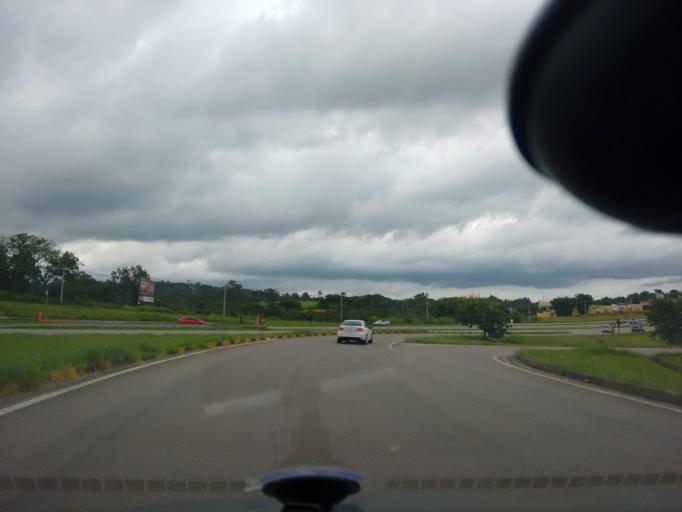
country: BR
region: Sao Paulo
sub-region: Indaiatuba
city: Indaiatuba
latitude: -23.0867
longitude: -47.1778
